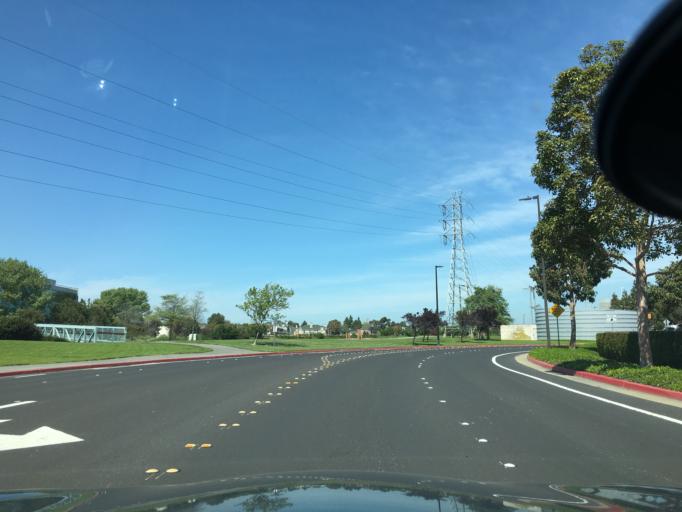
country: US
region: California
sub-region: San Mateo County
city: Belmont
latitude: 37.5295
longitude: -122.2672
